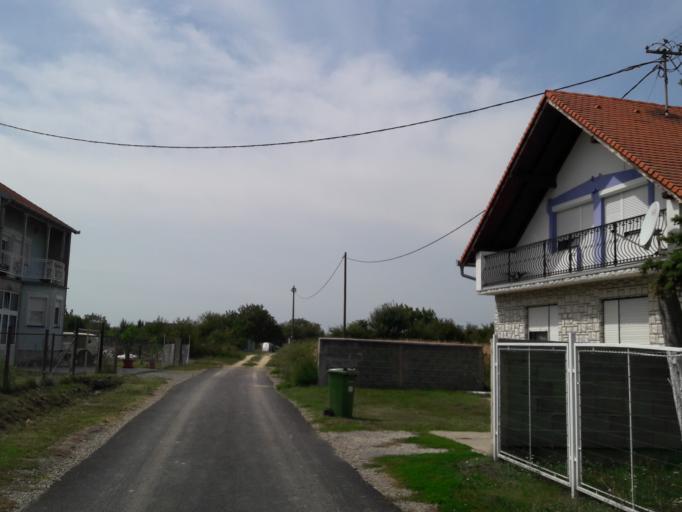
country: HR
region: Osjecko-Baranjska
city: Cepin
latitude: 45.5299
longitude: 18.5777
